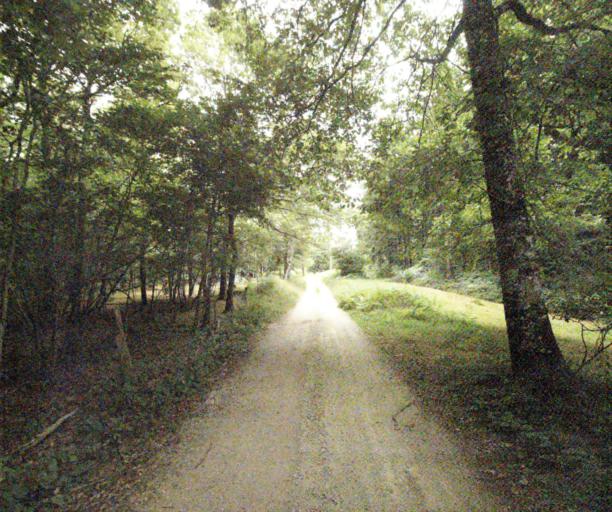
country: FR
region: Midi-Pyrenees
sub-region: Departement du Tarn
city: Soreze
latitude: 43.4253
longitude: 2.1066
